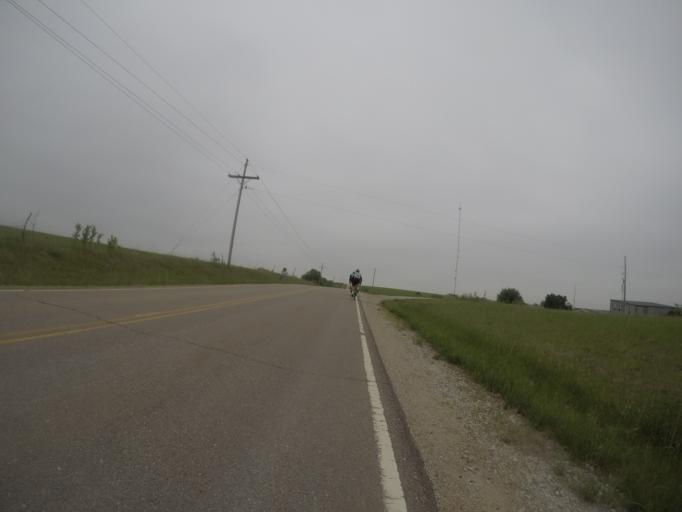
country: US
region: Kansas
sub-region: Pottawatomie County
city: Westmoreland
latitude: 39.5222
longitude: -96.3130
